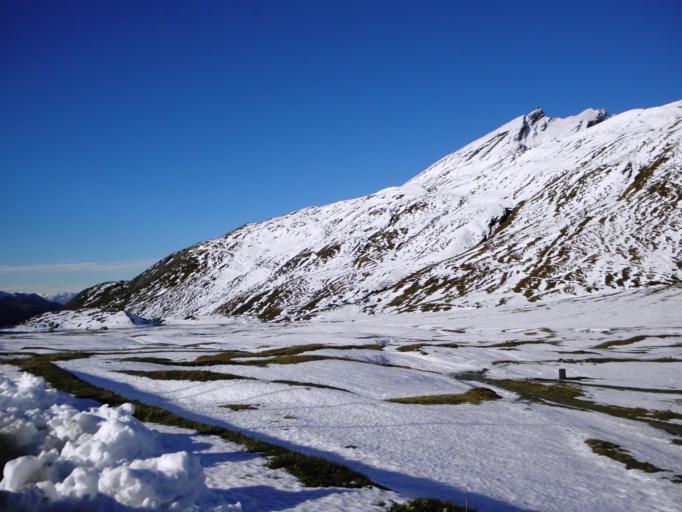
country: IT
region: Aosta Valley
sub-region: Valle d'Aosta
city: La Thuile
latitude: 45.6809
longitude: 6.8843
